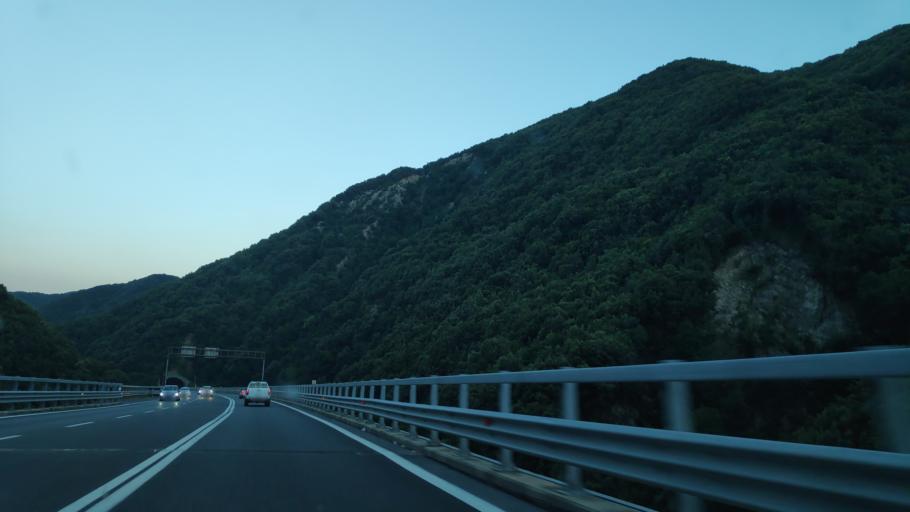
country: IT
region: Calabria
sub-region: Provincia di Reggio Calabria
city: Amato
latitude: 38.3689
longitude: 16.1831
